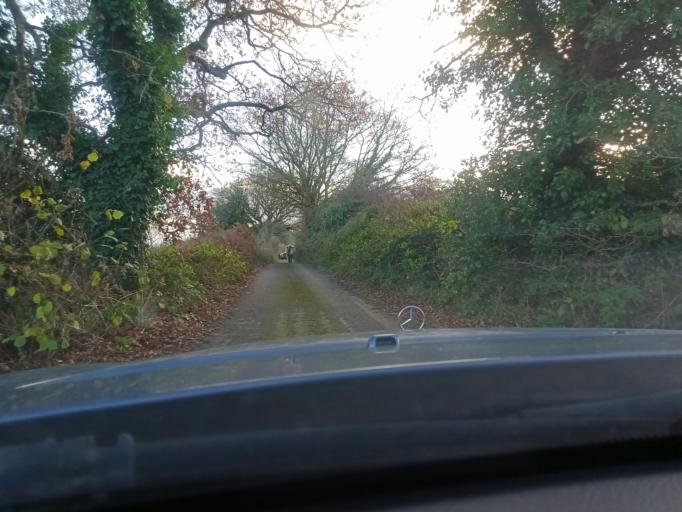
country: IE
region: Leinster
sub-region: Kilkenny
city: Graiguenamanagh
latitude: 52.4953
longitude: -6.9440
